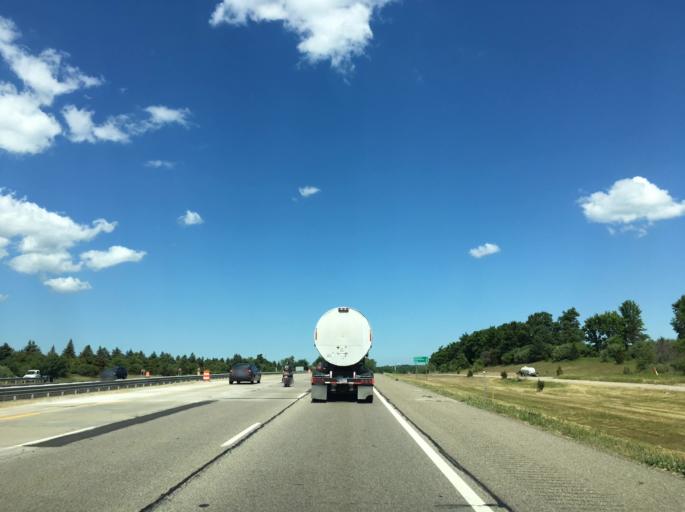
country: US
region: Michigan
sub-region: Oakland County
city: Pontiac
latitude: 42.7082
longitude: -83.3299
